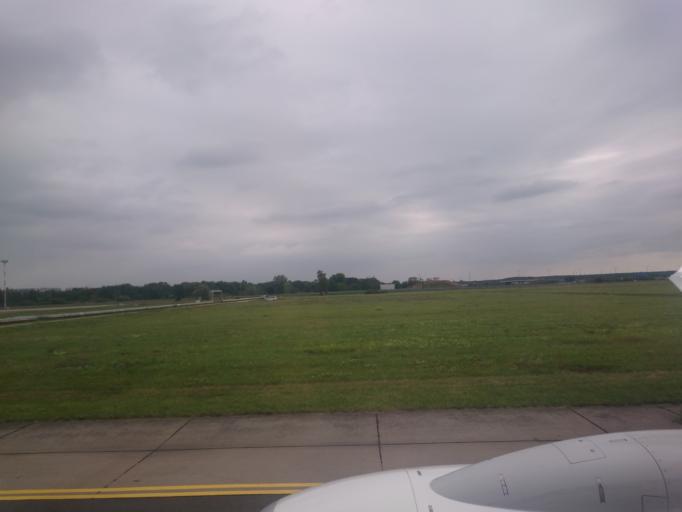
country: DE
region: Brandenburg
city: Schonefeld
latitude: 52.3853
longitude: 13.5225
